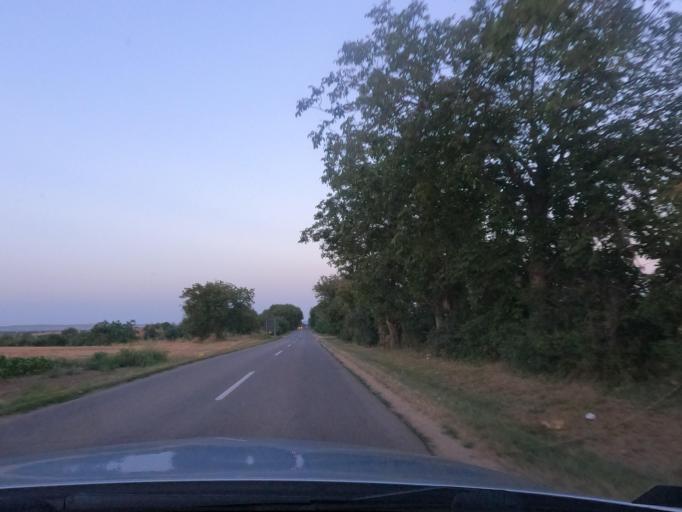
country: RS
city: Beska
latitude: 45.1125
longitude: 20.0370
